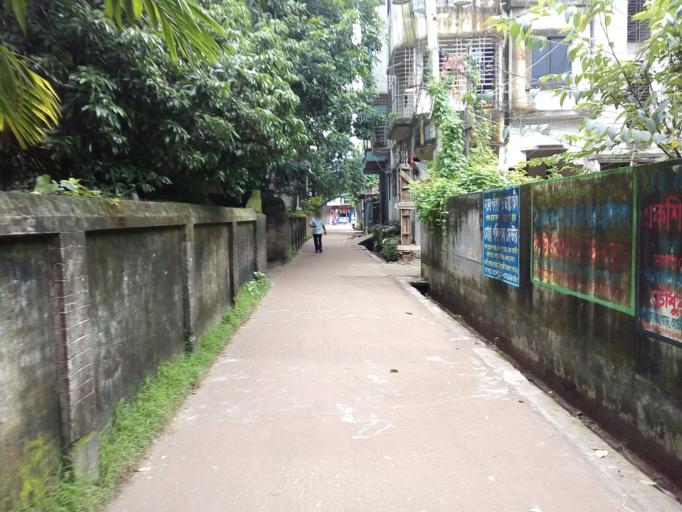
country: BD
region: Dhaka
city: Tungi
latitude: 23.8398
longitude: 90.2531
